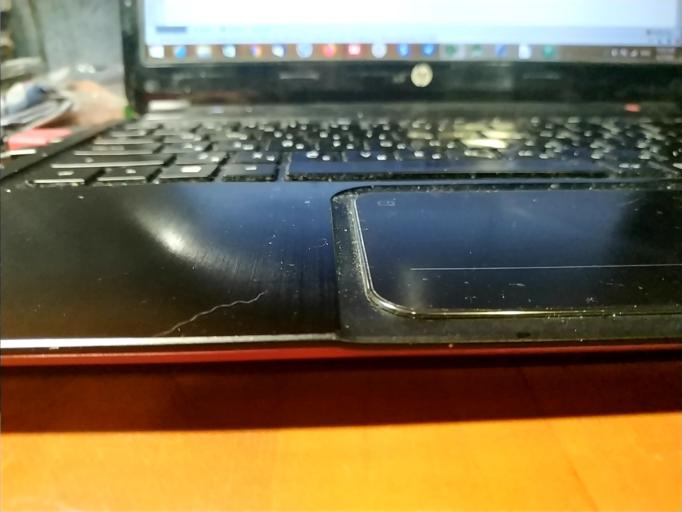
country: RU
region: Vologda
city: Suda
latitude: 58.9140
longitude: 37.5432
